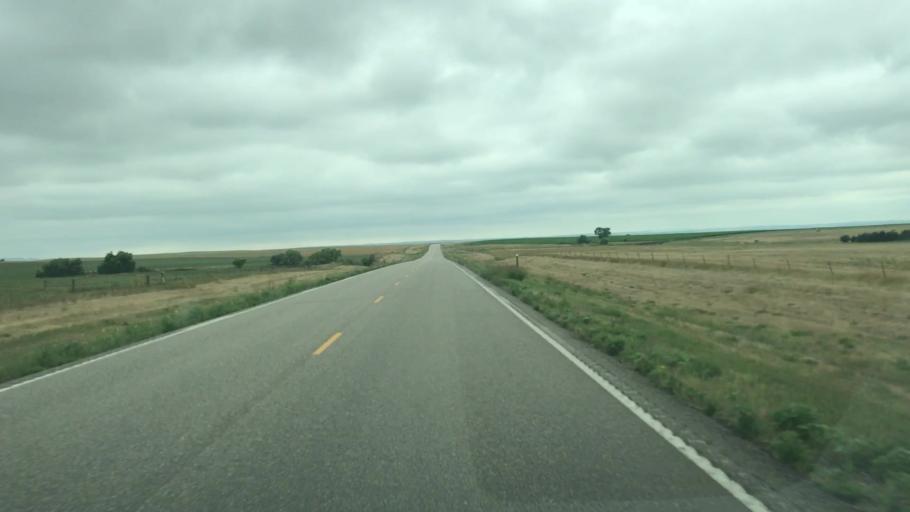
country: US
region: South Dakota
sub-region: Jackson County
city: Kadoka
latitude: 43.8193
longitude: -101.5224
